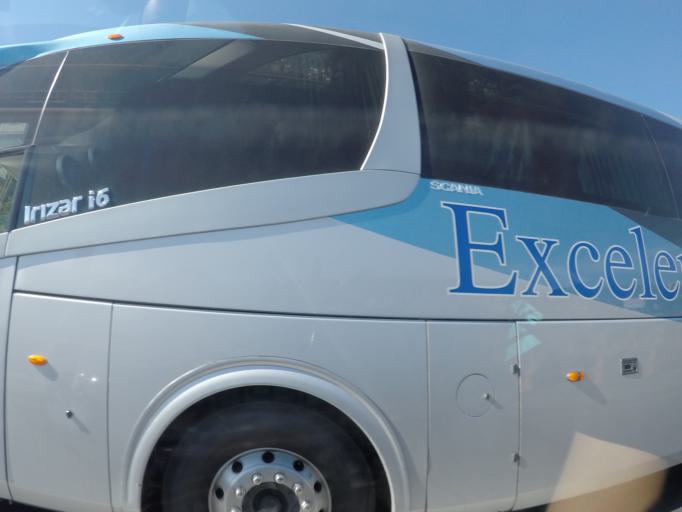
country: MX
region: Mexico City
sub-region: Cuajimalpa de Morelos
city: San Lorenzo Acopilco
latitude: 19.3212
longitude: -99.3349
